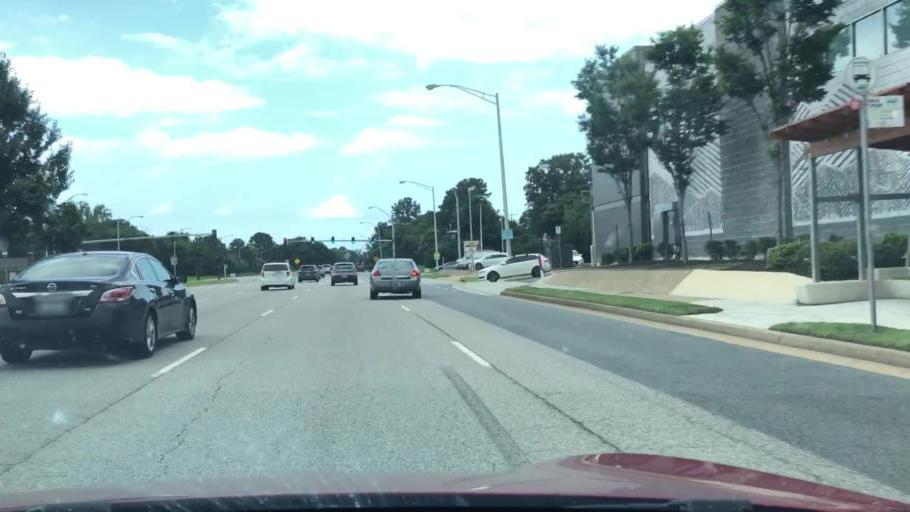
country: US
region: Virginia
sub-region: City of Chesapeake
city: Chesapeake
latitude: 36.8466
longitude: -76.1366
